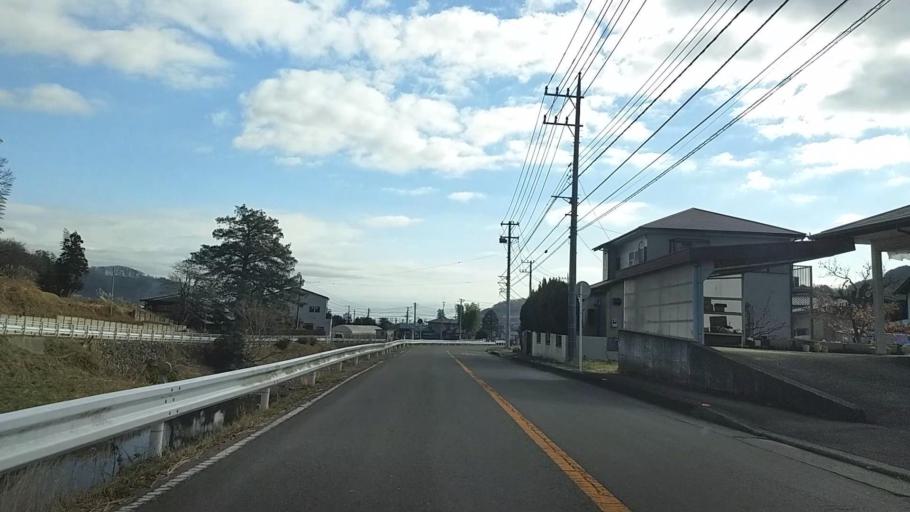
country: JP
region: Kanagawa
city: Isehara
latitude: 35.4369
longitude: 139.3051
